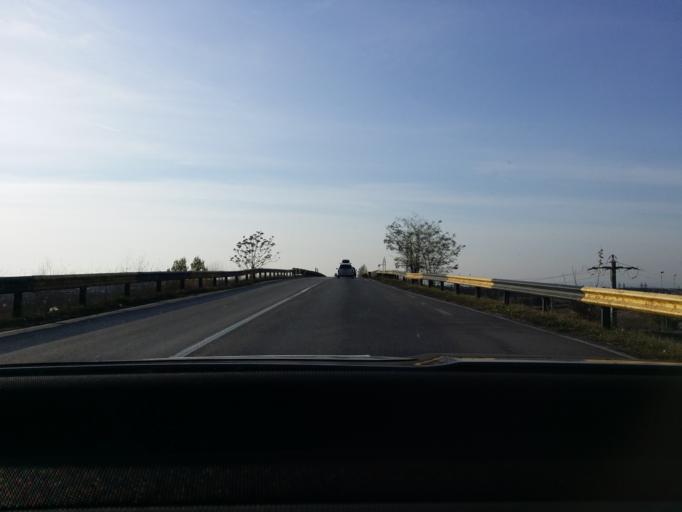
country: RO
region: Prahova
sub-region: Comuna Targsoru Vechi
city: Strejnicu
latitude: 44.9400
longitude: 25.9689
